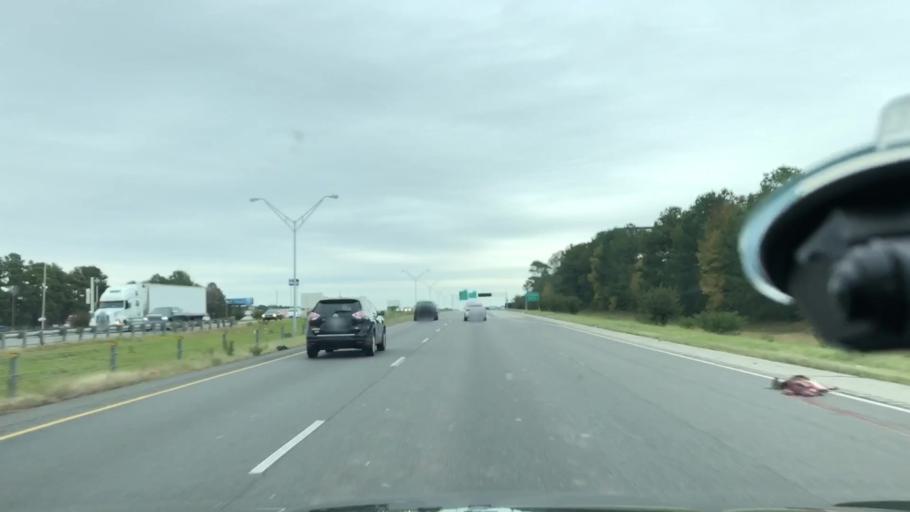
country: US
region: Arkansas
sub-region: Miller County
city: Texarkana
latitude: 33.4721
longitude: -94.0247
